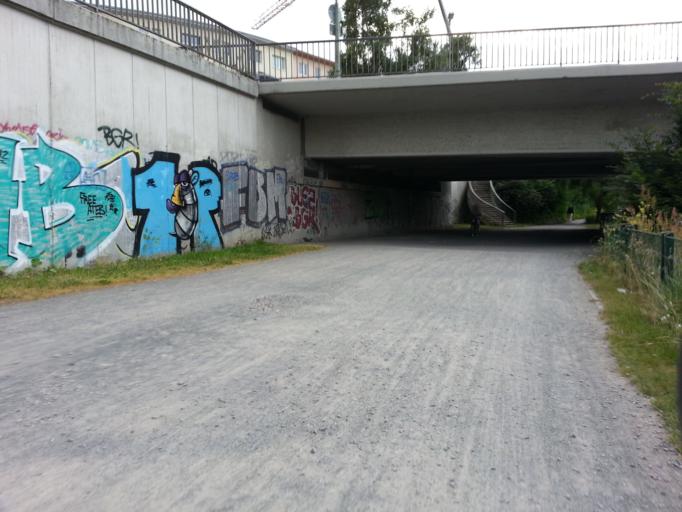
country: DE
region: Berlin
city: Charlottenburg-Nord
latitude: 52.5204
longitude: 13.3067
